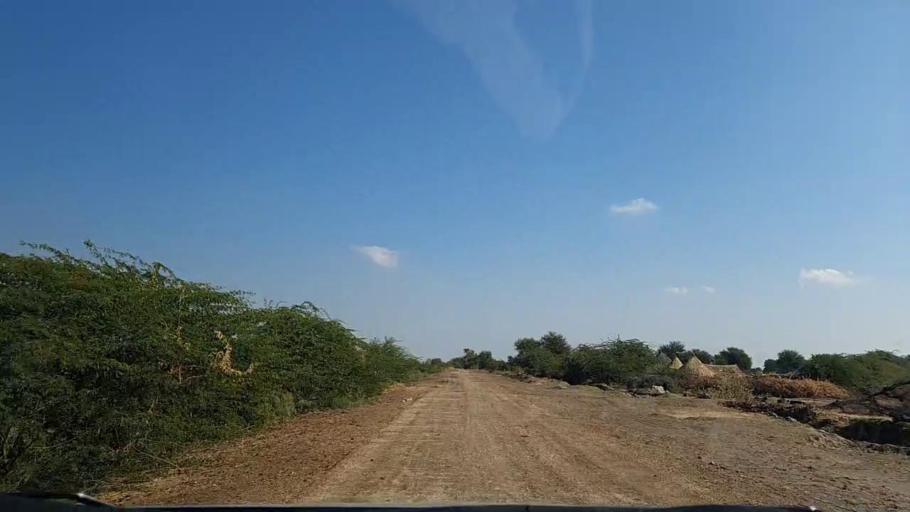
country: PK
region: Sindh
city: Pithoro
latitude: 25.6899
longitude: 69.3741
